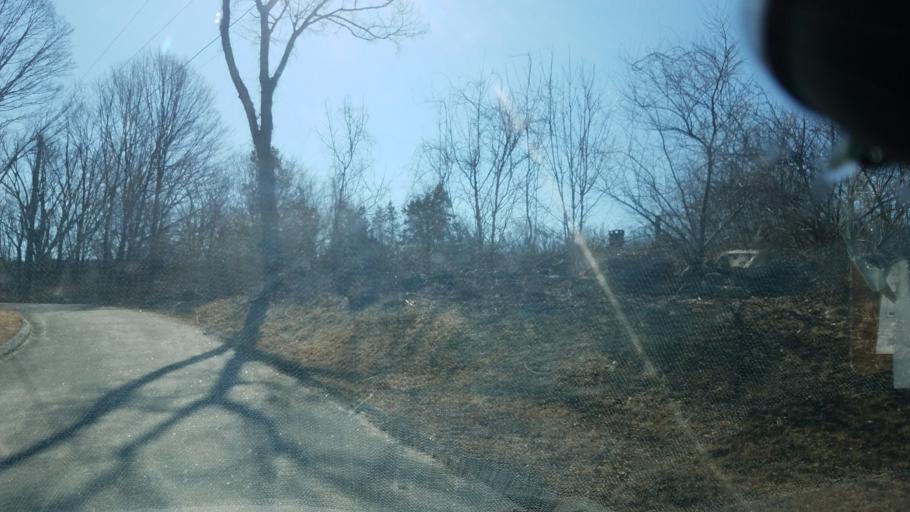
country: US
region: Connecticut
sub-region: Fairfield County
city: Newtown
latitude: 41.3557
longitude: -73.3099
